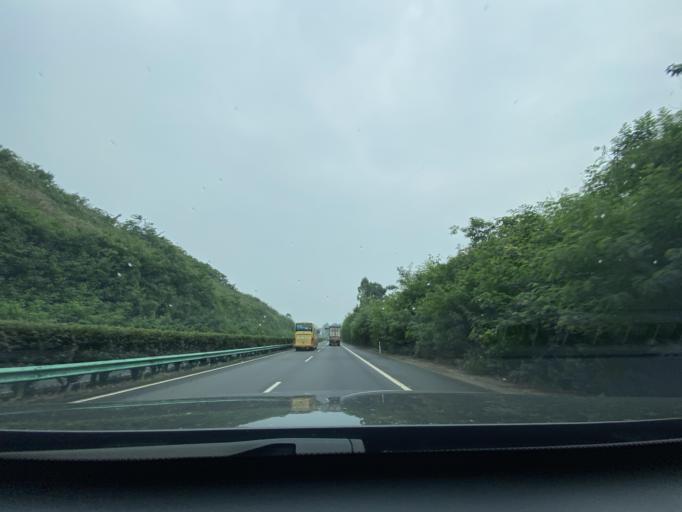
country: CN
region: Sichuan
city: Longquan
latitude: 30.3004
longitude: 104.1212
